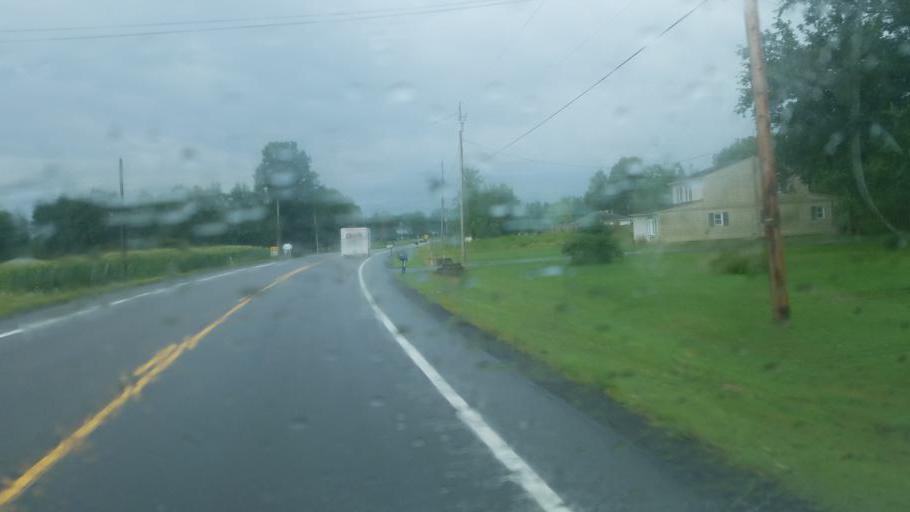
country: US
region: Ohio
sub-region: Trumbull County
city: Champion Heights
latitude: 41.3515
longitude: -80.8585
